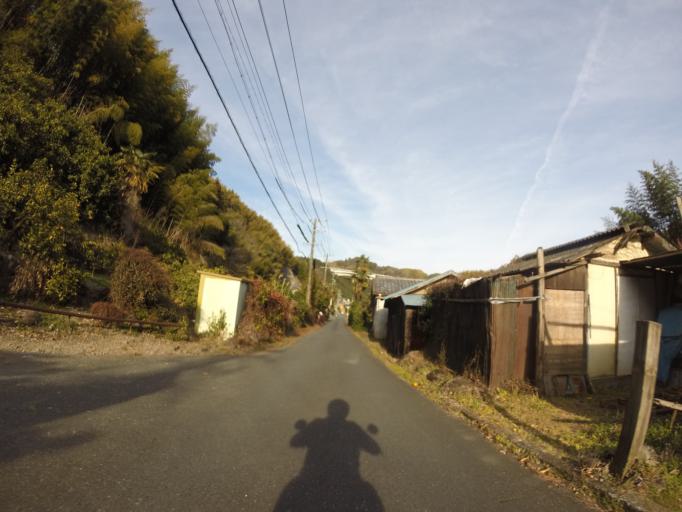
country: JP
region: Shizuoka
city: Shizuoka-shi
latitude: 35.0703
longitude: 138.4583
